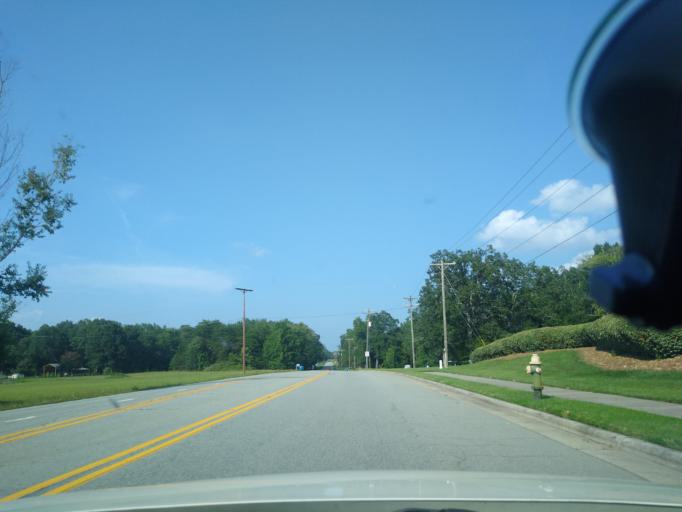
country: US
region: North Carolina
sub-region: Guilford County
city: McLeansville
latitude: 36.0988
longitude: -79.6671
